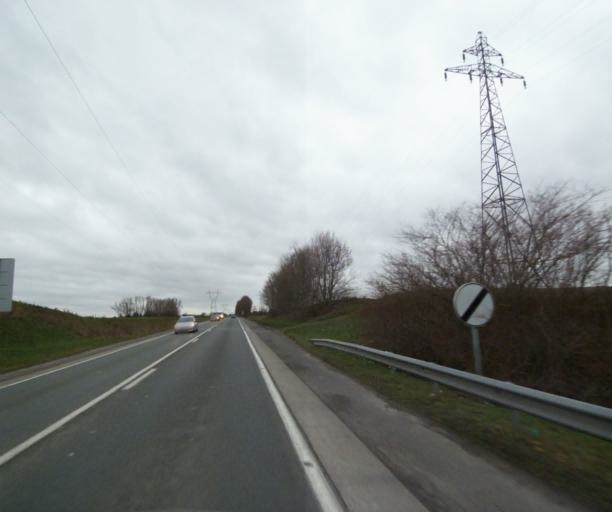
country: FR
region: Nord-Pas-de-Calais
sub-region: Departement du Nord
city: Marly
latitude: 50.3536
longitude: 3.5591
